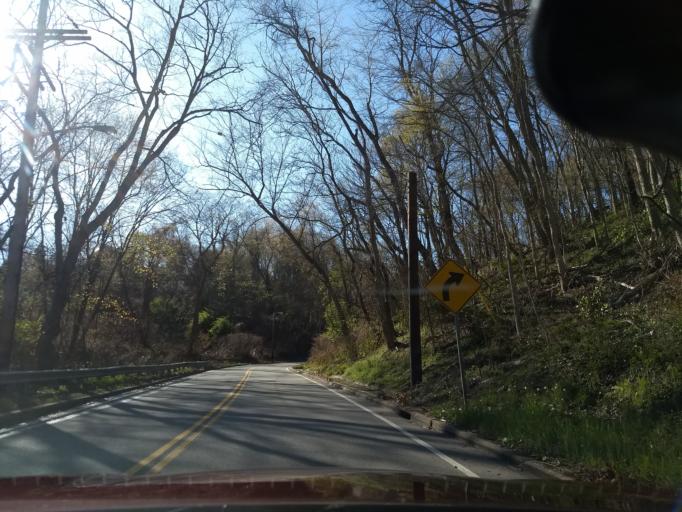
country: US
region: Pennsylvania
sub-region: Allegheny County
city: Mount Oliver
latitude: 40.4069
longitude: -79.9798
